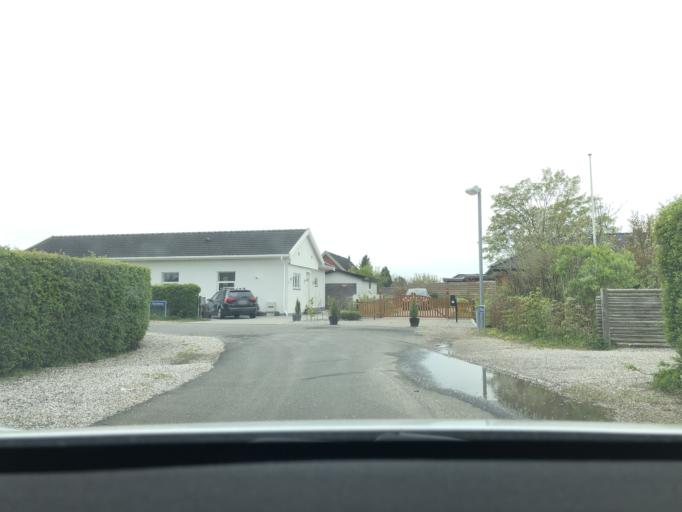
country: DK
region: Zealand
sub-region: Greve Kommune
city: Greve
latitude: 55.5713
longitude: 12.2750
